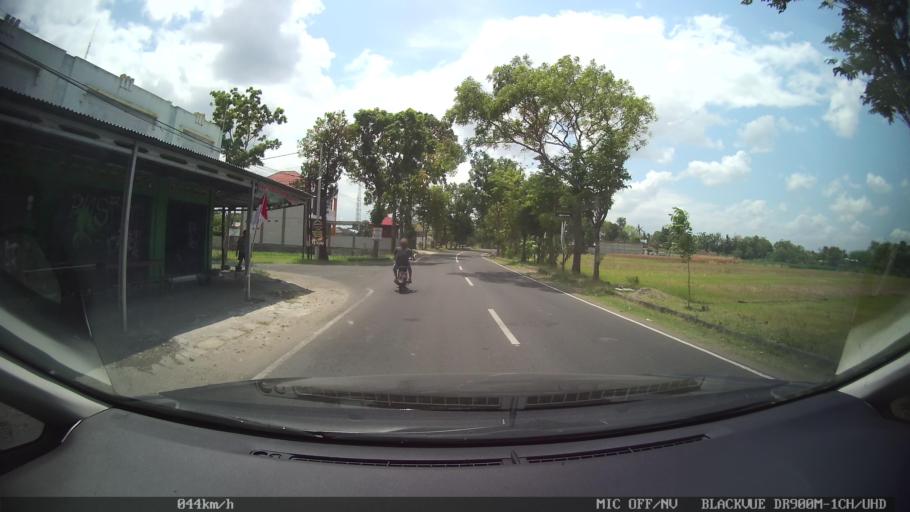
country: ID
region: Daerah Istimewa Yogyakarta
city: Bantul
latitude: -7.8878
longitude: 110.3338
